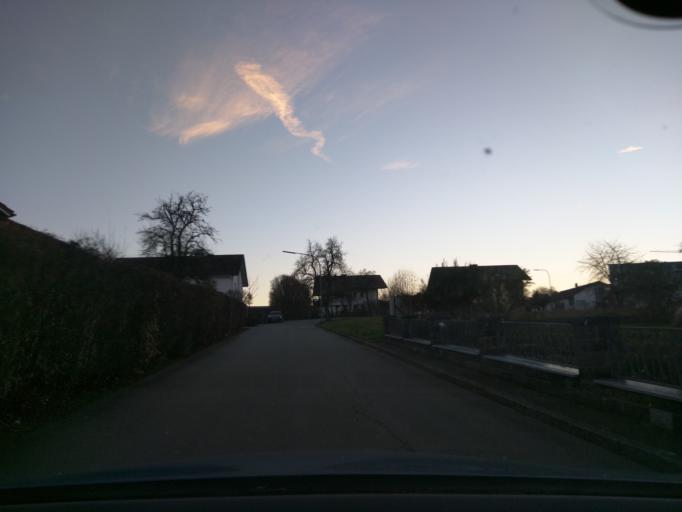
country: DE
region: Bavaria
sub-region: Lower Bavaria
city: Passau
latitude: 48.5778
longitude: 13.4019
